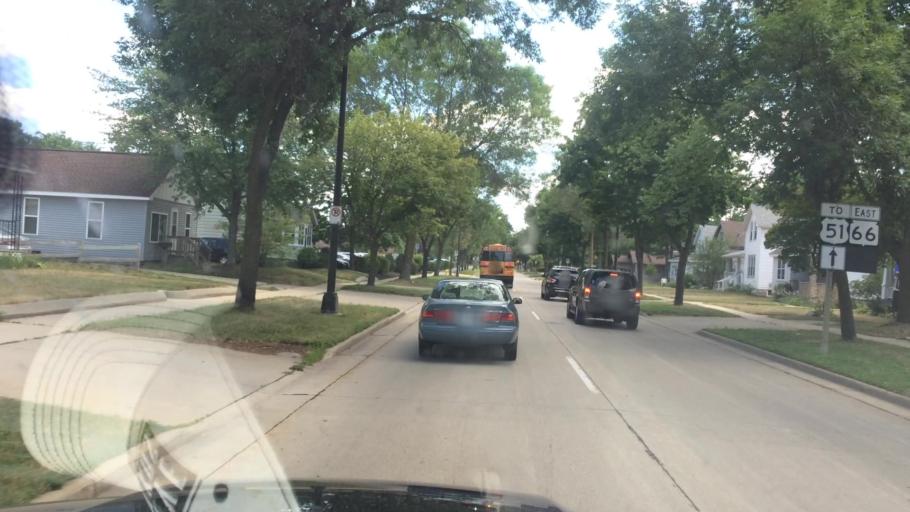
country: US
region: Wisconsin
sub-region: Portage County
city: Stevens Point
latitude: 44.5224
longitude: -89.5644
